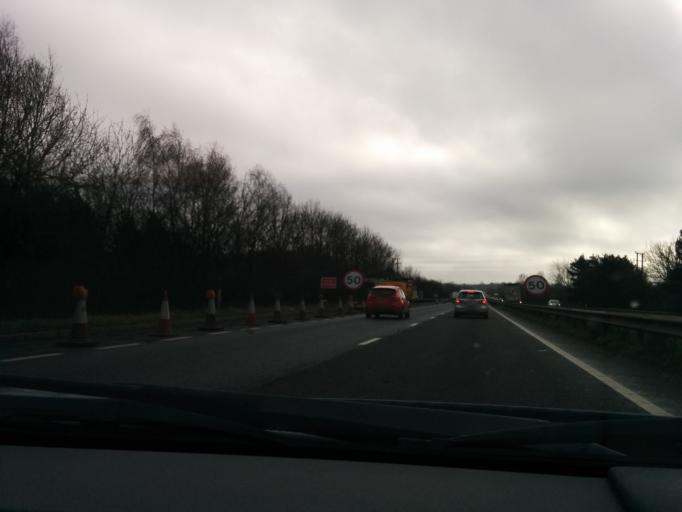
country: GB
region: England
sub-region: Oxfordshire
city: Sutton Courtenay
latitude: 51.6339
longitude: -1.3139
